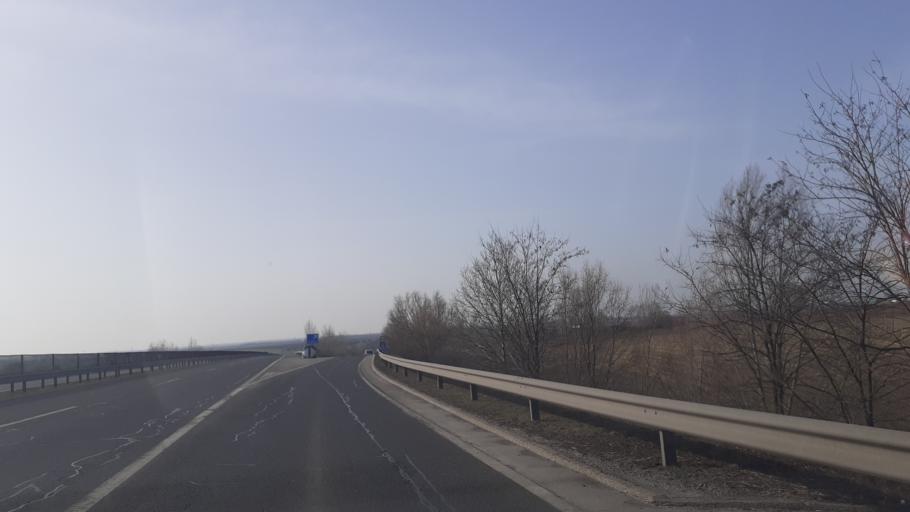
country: HU
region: Fejer
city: Baracs
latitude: 46.9099
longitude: 18.9317
